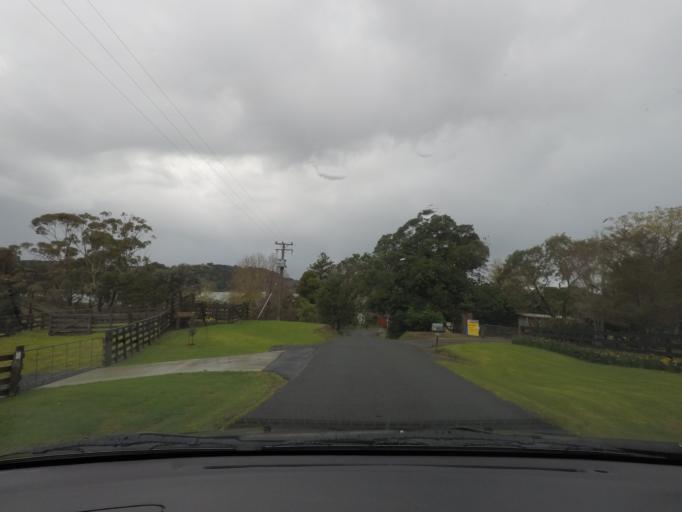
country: NZ
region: Auckland
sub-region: Auckland
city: Warkworth
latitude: -36.4722
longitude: 174.7349
